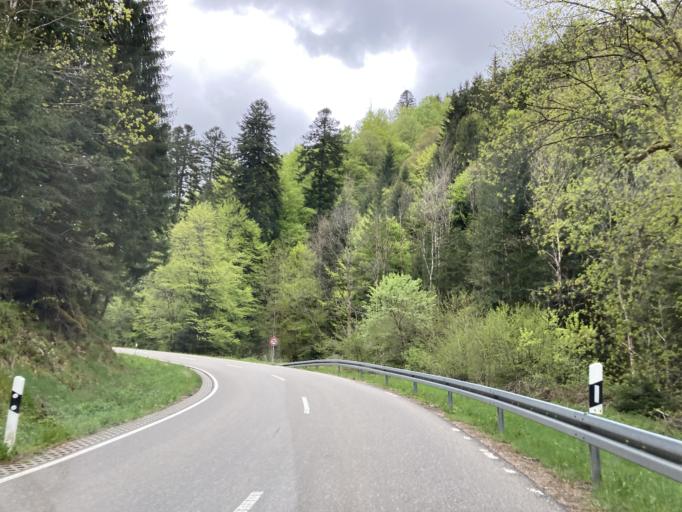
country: DE
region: Baden-Wuerttemberg
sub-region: Freiburg Region
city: Schonach im Schwarzwald
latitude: 48.1546
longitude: 8.1585
